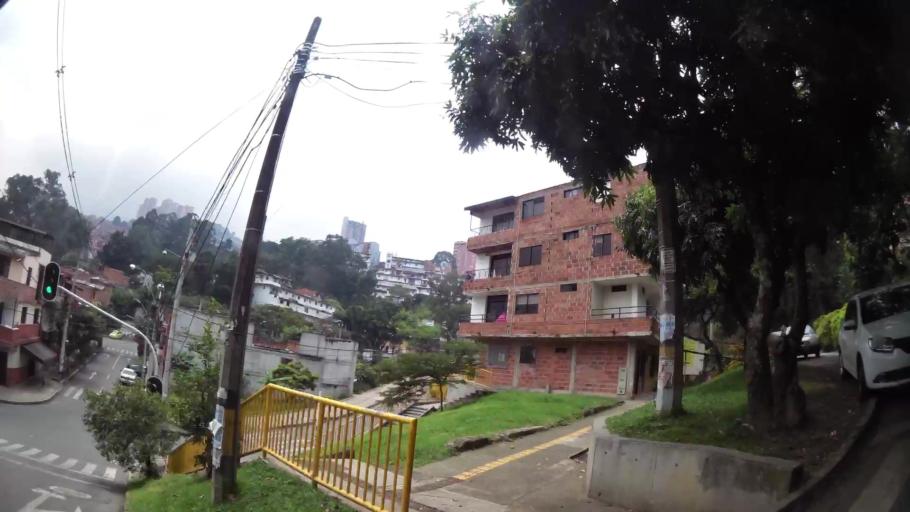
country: CO
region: Antioquia
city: Medellin
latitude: 6.2357
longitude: -75.5638
